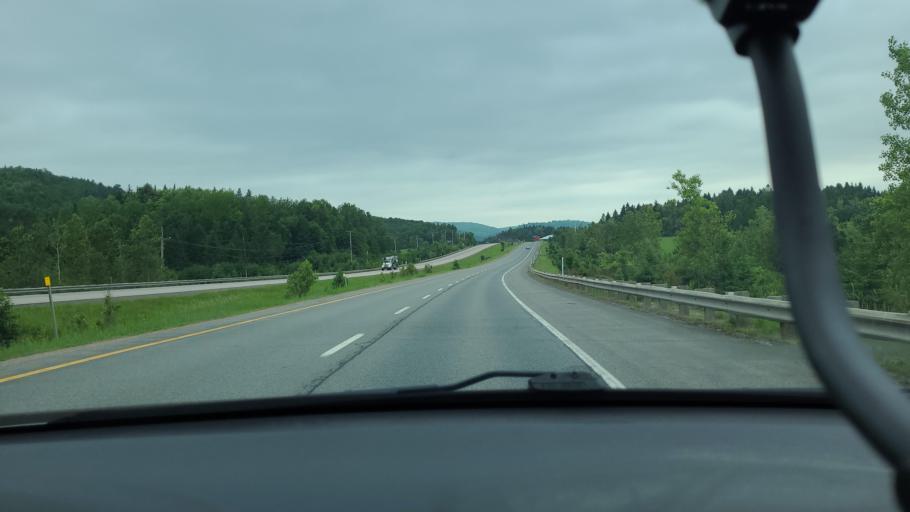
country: CA
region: Quebec
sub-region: Laurentides
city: Labelle
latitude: 46.1672
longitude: -74.7137
